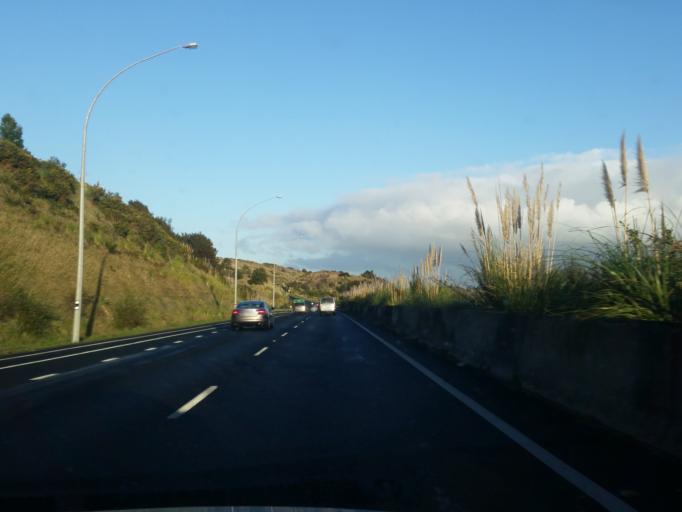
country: NZ
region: Auckland
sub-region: Auckland
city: Pukekohe East
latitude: -37.2831
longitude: 175.0507
